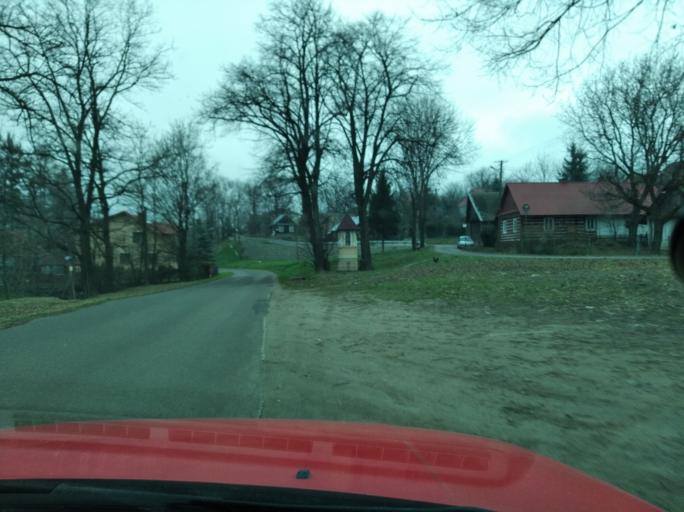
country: PL
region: Subcarpathian Voivodeship
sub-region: Powiat przeworski
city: Rozborz
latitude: 50.0570
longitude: 22.5457
